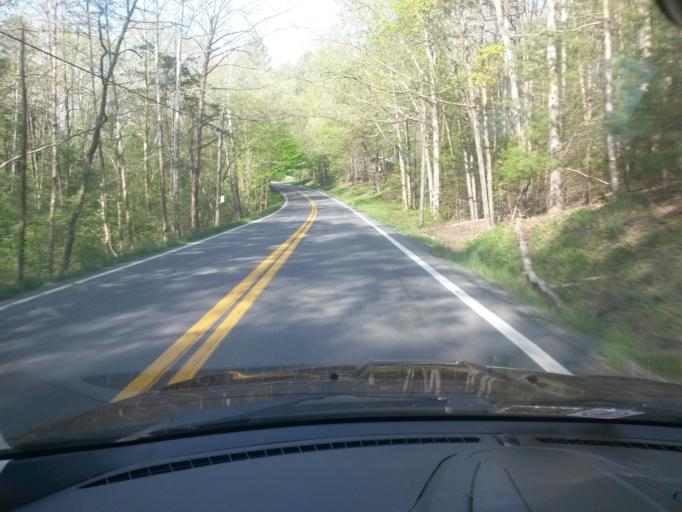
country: US
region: Virginia
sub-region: City of Covington
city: Covington
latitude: 37.9910
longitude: -80.0861
